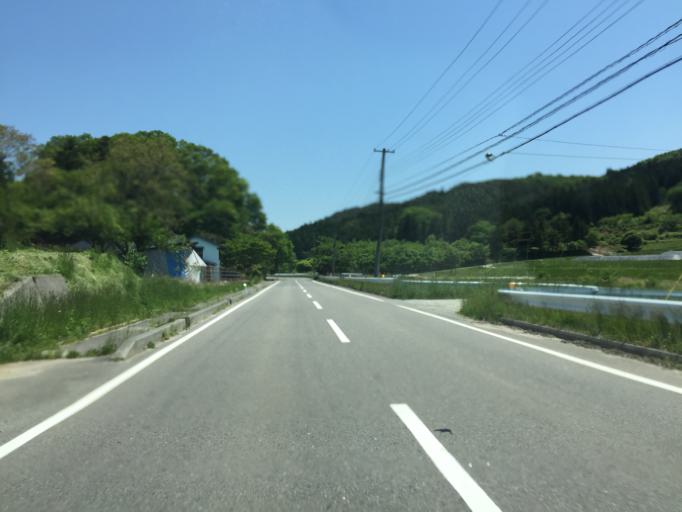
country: JP
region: Fukushima
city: Funehikimachi-funehiki
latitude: 37.5043
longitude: 140.7435
